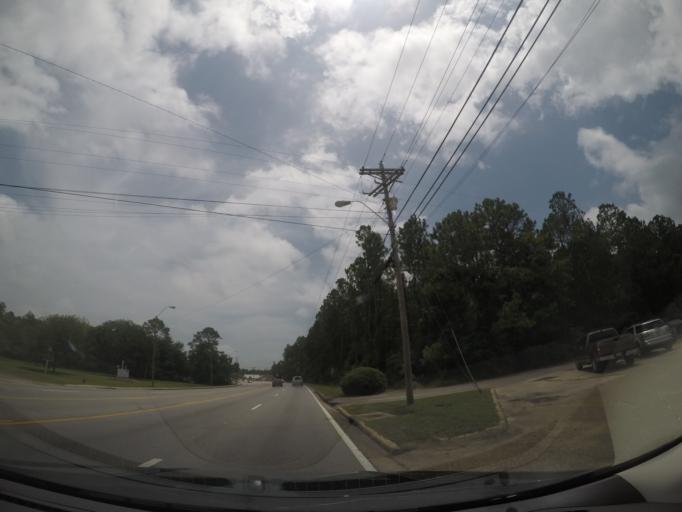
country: US
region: Mississippi
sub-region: Jackson County
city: Gautier
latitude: 30.4066
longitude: -88.6558
